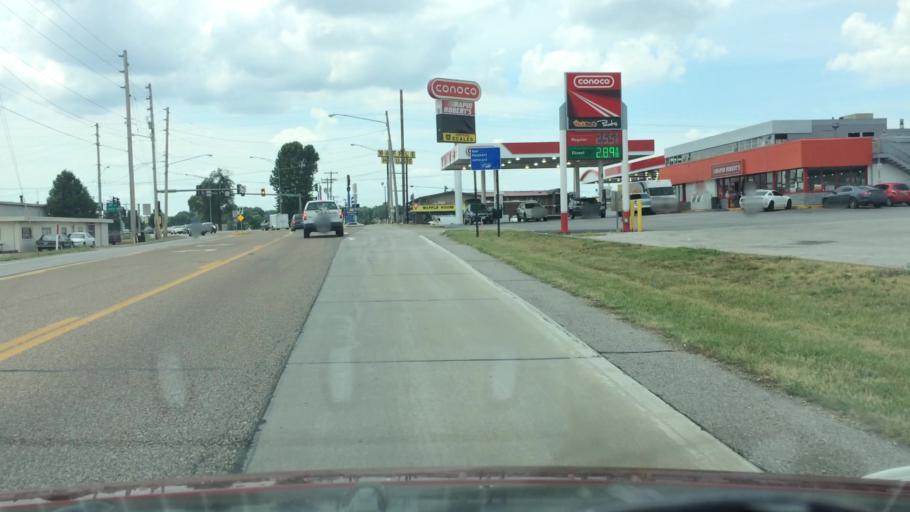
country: US
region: Missouri
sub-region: Greene County
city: Springfield
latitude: 37.2554
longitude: -93.2651
